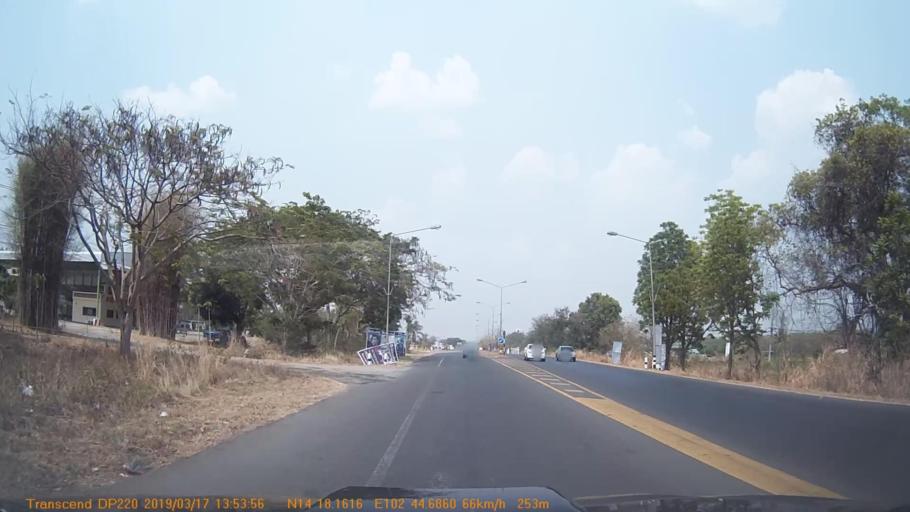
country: TH
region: Buriram
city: Non Din Daeng
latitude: 14.3029
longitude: 102.7448
